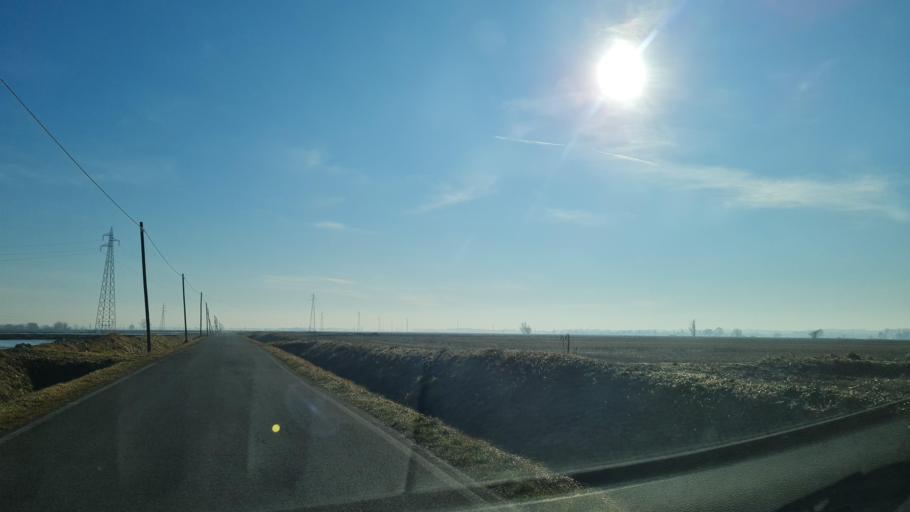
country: IT
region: Piedmont
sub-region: Provincia di Biella
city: Massazza
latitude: 45.4535
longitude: 8.1631
